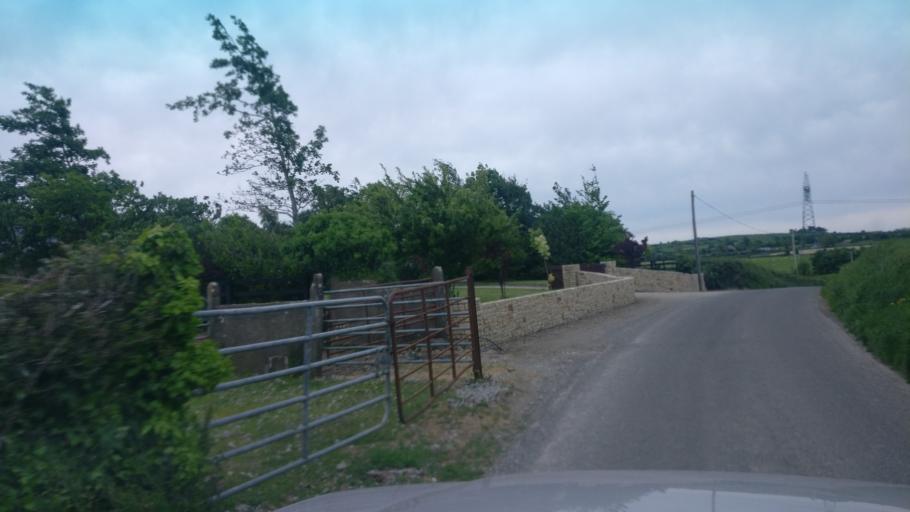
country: IE
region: Connaught
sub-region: County Galway
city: Portumna
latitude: 53.1311
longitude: -8.2900
